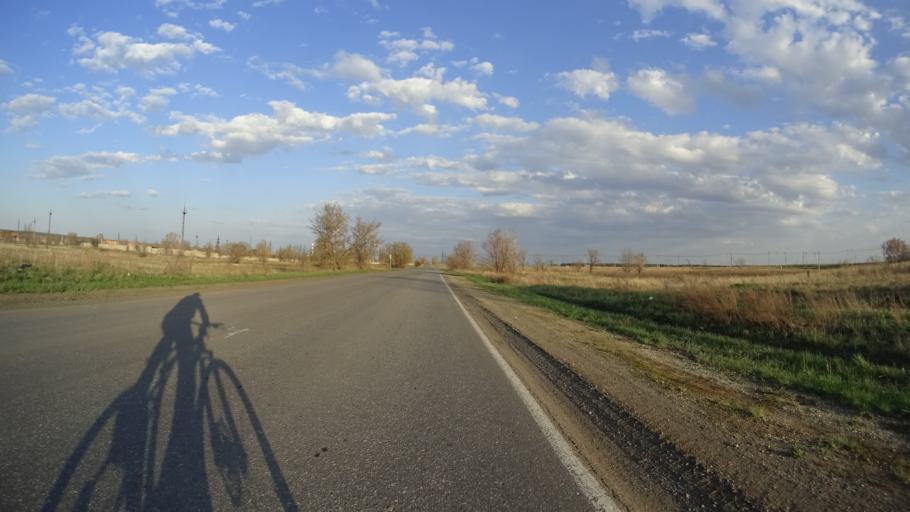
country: RU
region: Chelyabinsk
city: Troitsk
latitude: 54.0610
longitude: 61.5772
